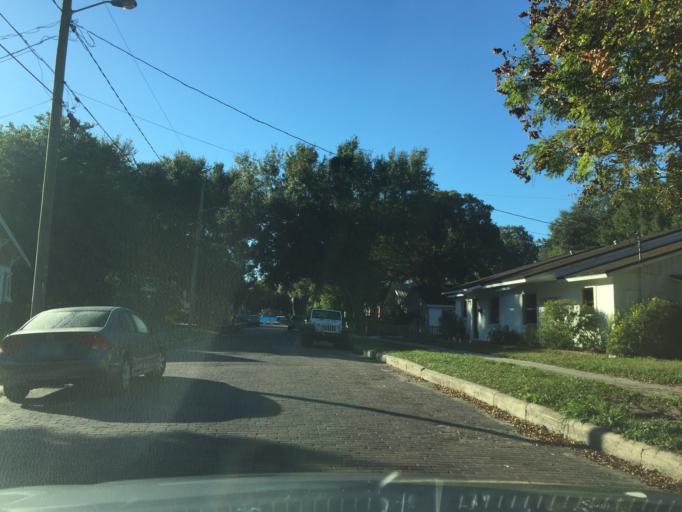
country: US
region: Florida
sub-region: Hillsborough County
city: Tampa
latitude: 27.9690
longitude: -82.4570
